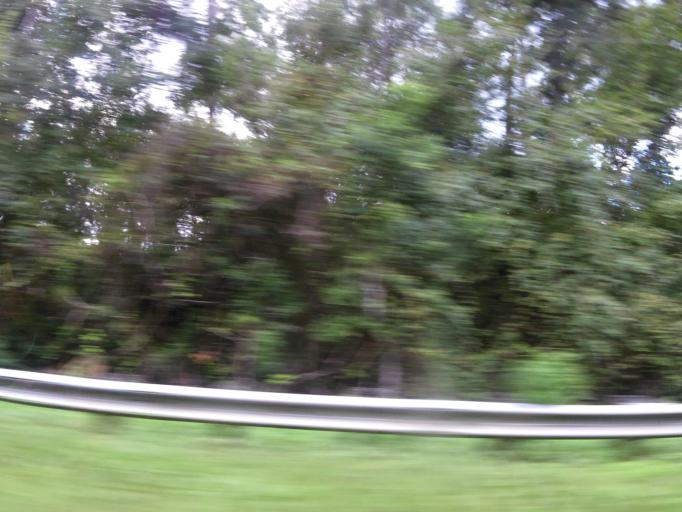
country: US
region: Florida
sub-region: Putnam County
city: East Palatka
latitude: 29.7713
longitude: -81.4801
